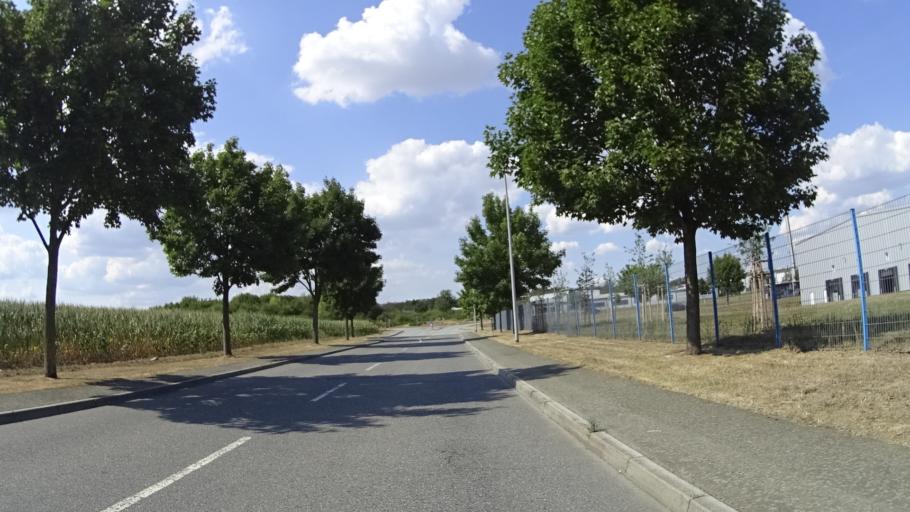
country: DE
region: Saxony
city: Zittau
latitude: 50.9062
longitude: 14.8391
